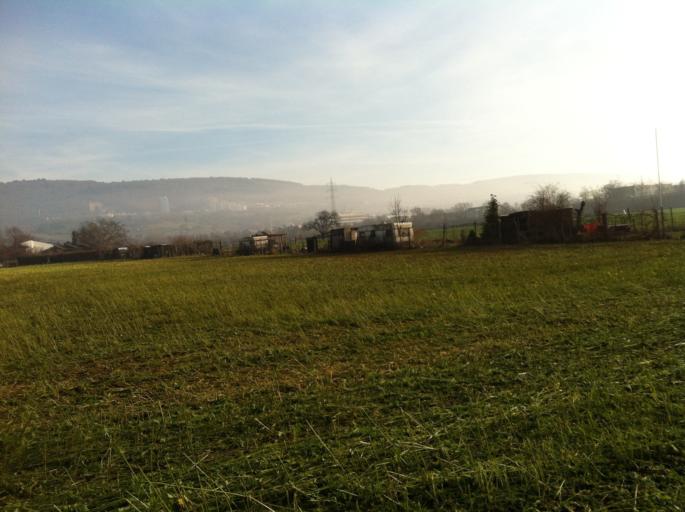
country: DE
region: Baden-Wuerttemberg
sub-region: Karlsruhe Region
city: Leimen
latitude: 49.3706
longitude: 8.6740
